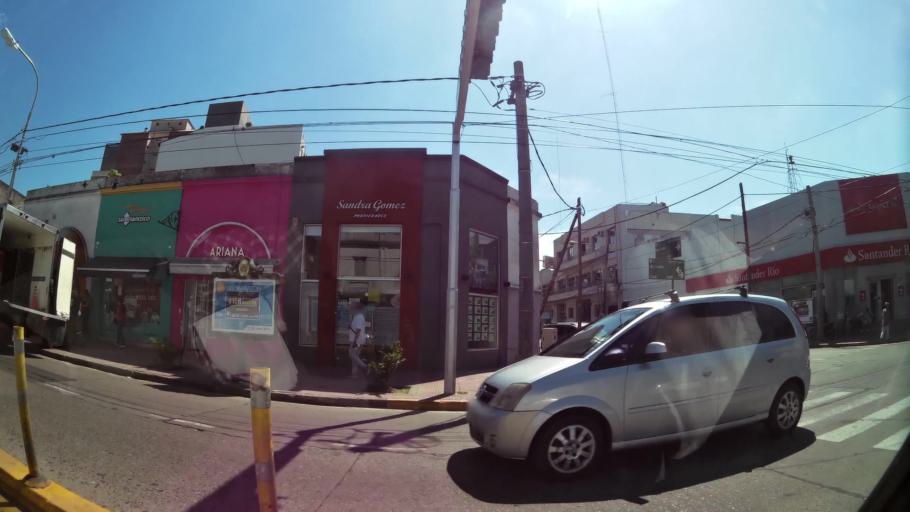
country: AR
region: Buenos Aires
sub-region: Partido de Tigre
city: Tigre
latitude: -34.4260
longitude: -58.5763
